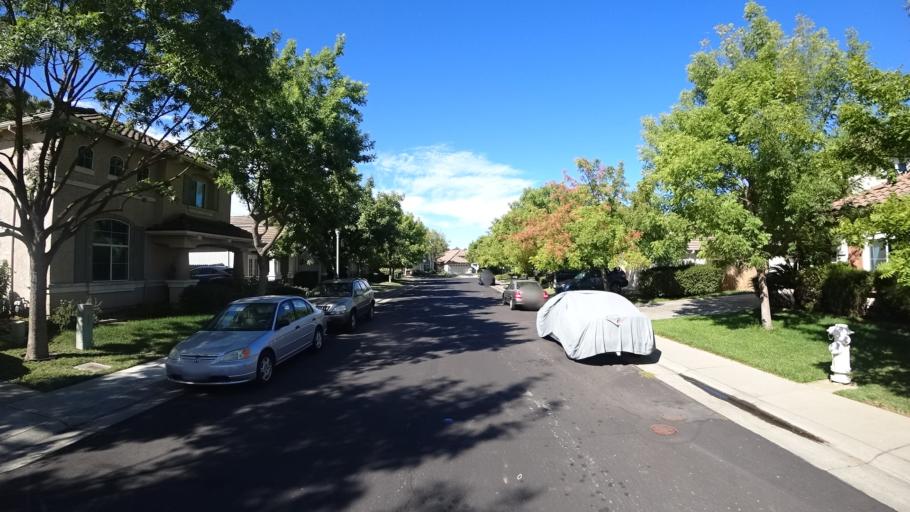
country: US
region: California
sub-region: Sacramento County
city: Laguna
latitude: 38.4268
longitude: -121.4781
